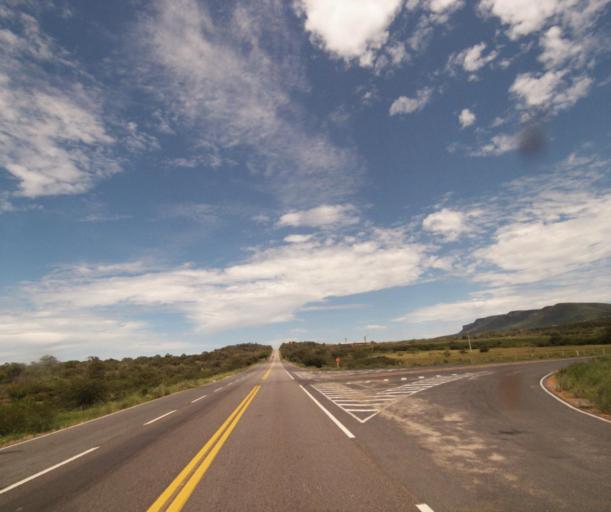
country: BR
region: Bahia
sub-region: Palmas De Monte Alto
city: Palmas de Monte Alto
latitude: -14.2512
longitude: -43.1839
